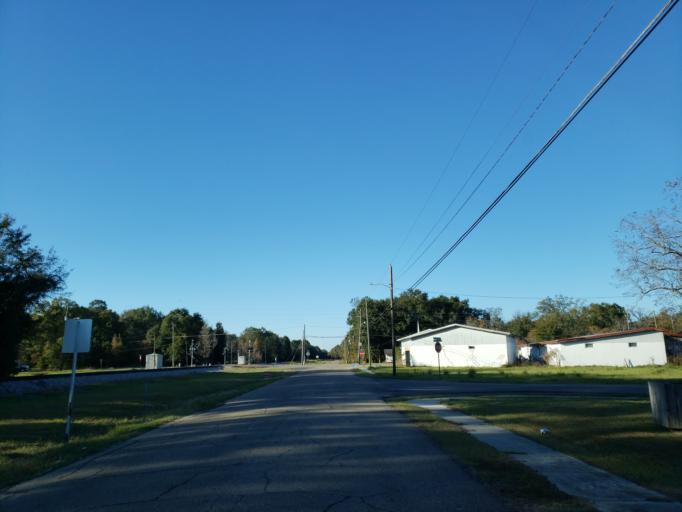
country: US
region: Mississippi
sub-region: Forrest County
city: Hattiesburg
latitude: 31.2769
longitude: -89.2652
